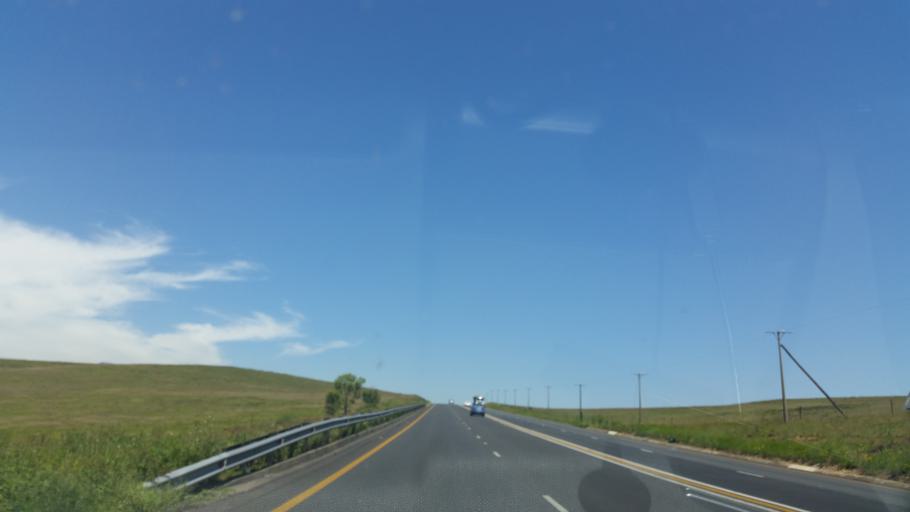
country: ZA
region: Orange Free State
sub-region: Thabo Mofutsanyana District Municipality
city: Harrismith
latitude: -28.3665
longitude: 29.3519
